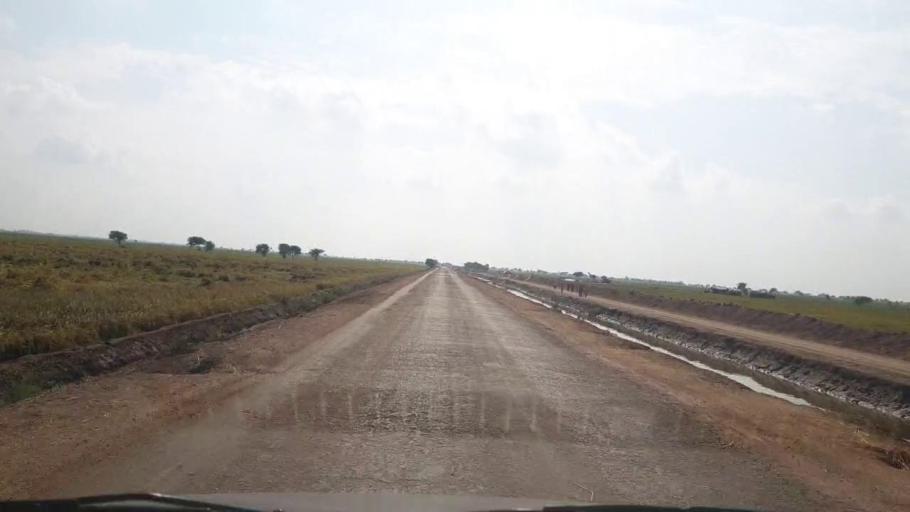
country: PK
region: Sindh
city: Kario
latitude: 24.5816
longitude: 68.5782
